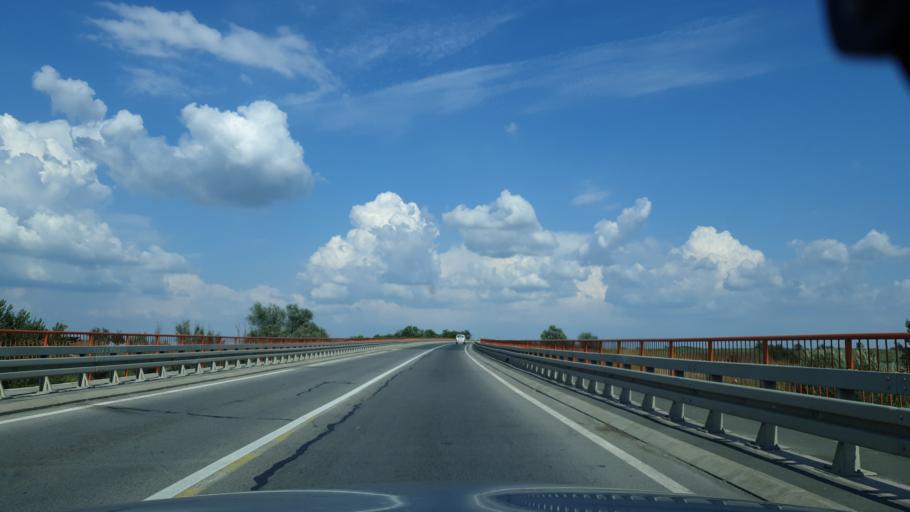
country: RS
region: Autonomna Pokrajina Vojvodina
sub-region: Juznobacki Okrug
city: Petrovaradin
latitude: 45.3067
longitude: 19.8685
